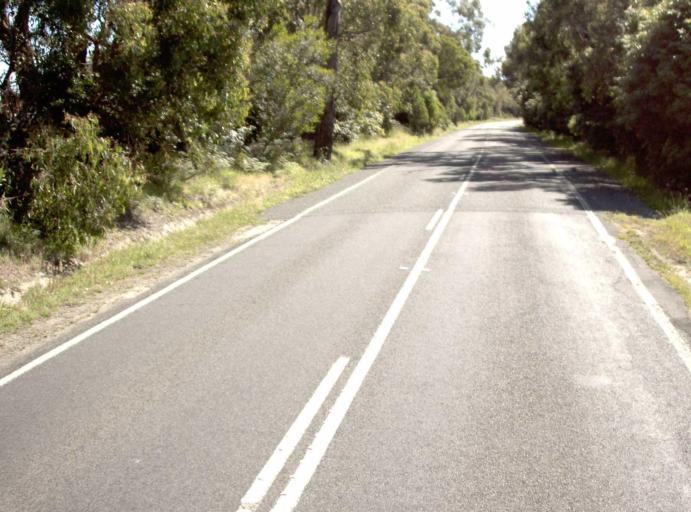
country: AU
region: Victoria
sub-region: Latrobe
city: Morwell
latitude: -38.6673
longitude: 146.4050
